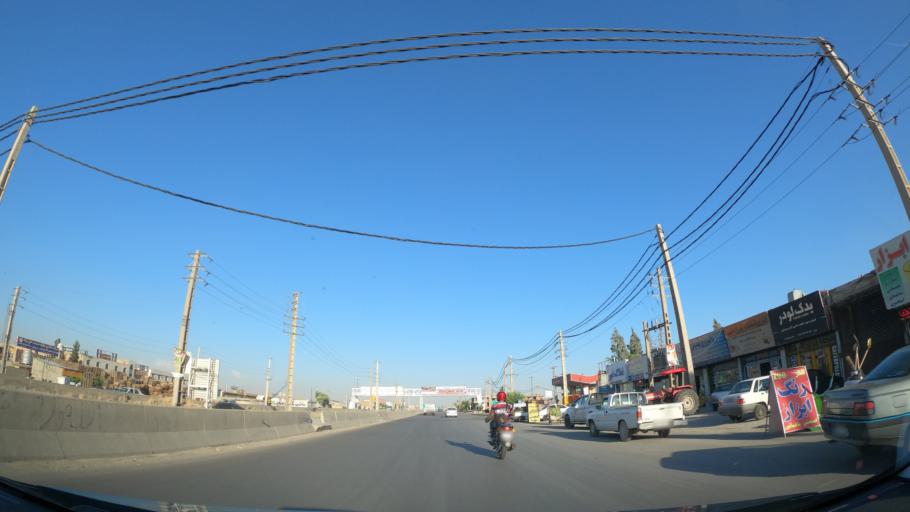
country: IR
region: Alborz
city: Hashtgerd
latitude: 35.9180
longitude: 50.7527
